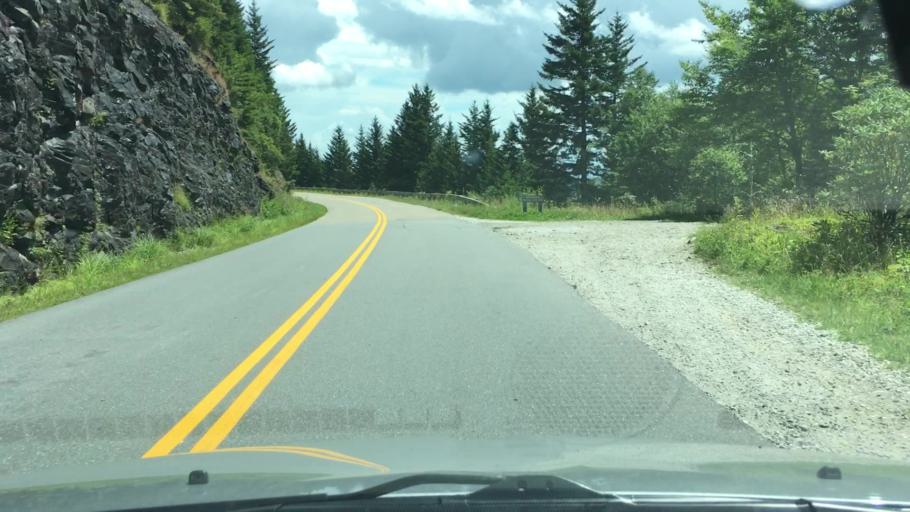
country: US
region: North Carolina
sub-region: Buncombe County
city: Black Mountain
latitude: 35.7311
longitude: -82.3141
